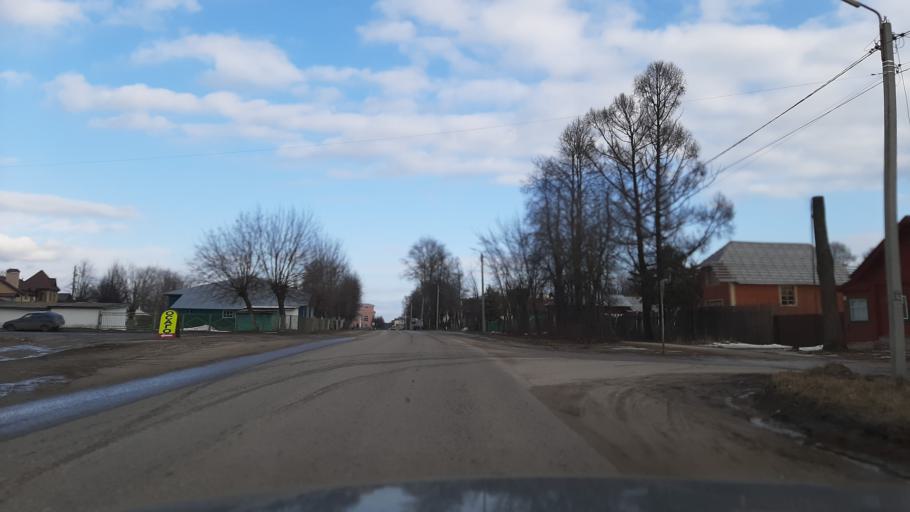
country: RU
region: Ivanovo
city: Teykovo
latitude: 56.8547
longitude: 40.5259
